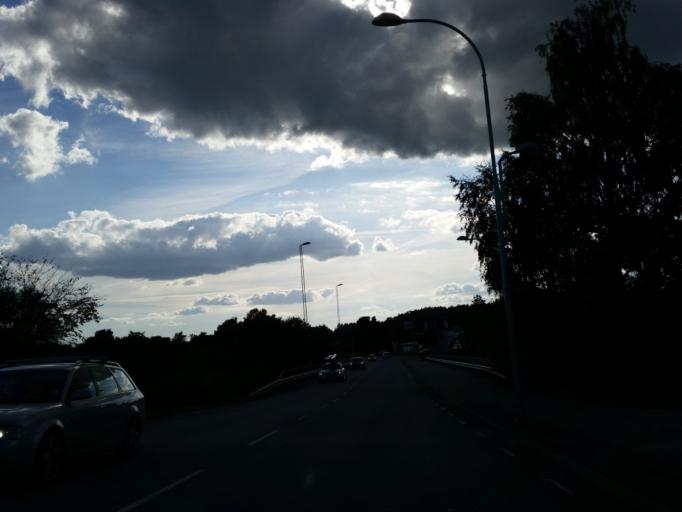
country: SE
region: Soedermanland
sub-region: Trosa Kommun
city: Vagnharad
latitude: 58.9450
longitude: 17.4921
